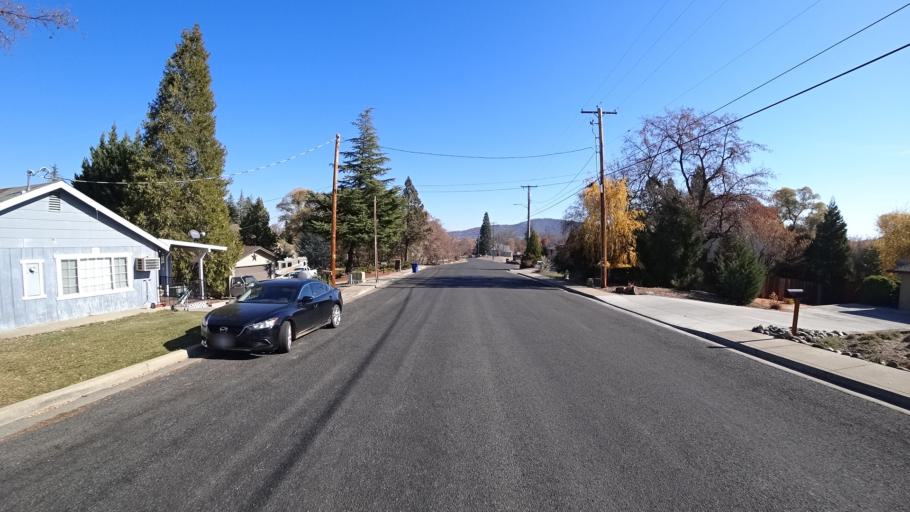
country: US
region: California
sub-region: Siskiyou County
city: Yreka
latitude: 41.7315
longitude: -122.6490
